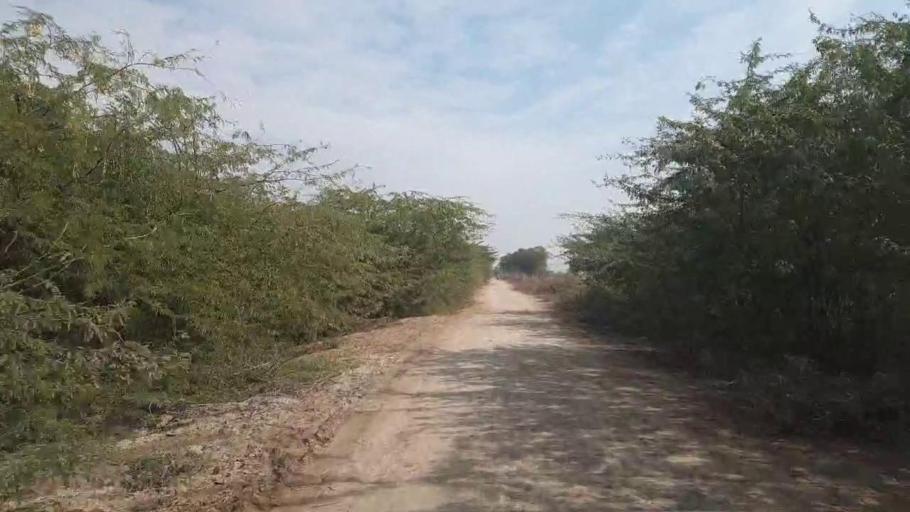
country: PK
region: Sindh
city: Nawabshah
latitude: 26.1140
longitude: 68.4874
